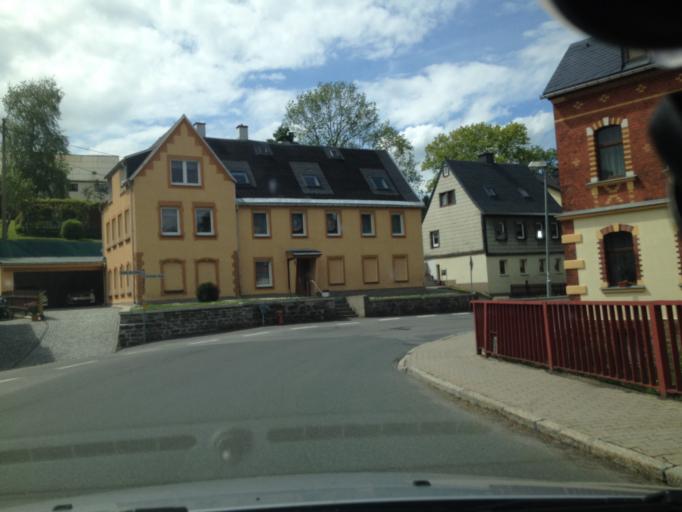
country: DE
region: Saxony
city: Crottendorf
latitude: 50.5312
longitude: 12.9951
